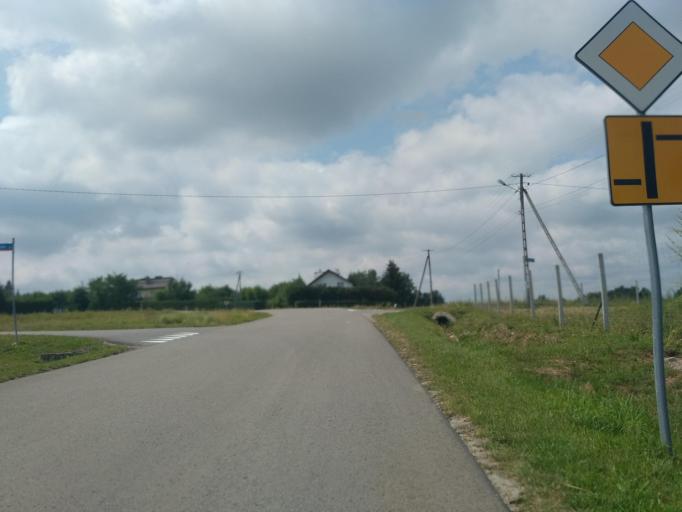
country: PL
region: Subcarpathian Voivodeship
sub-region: Powiat lancucki
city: Kraczkowa
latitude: 50.0154
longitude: 22.1630
